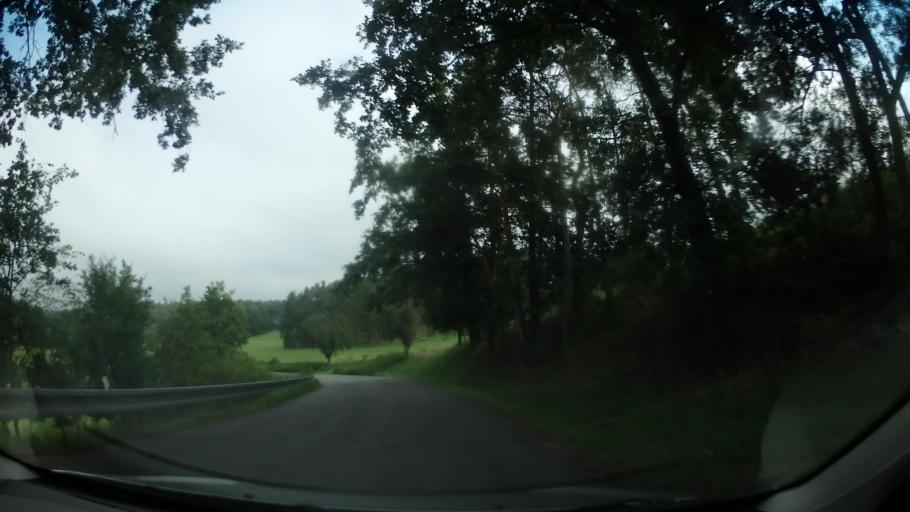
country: CZ
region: Central Bohemia
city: Sedlcany
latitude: 49.7085
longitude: 14.4251
